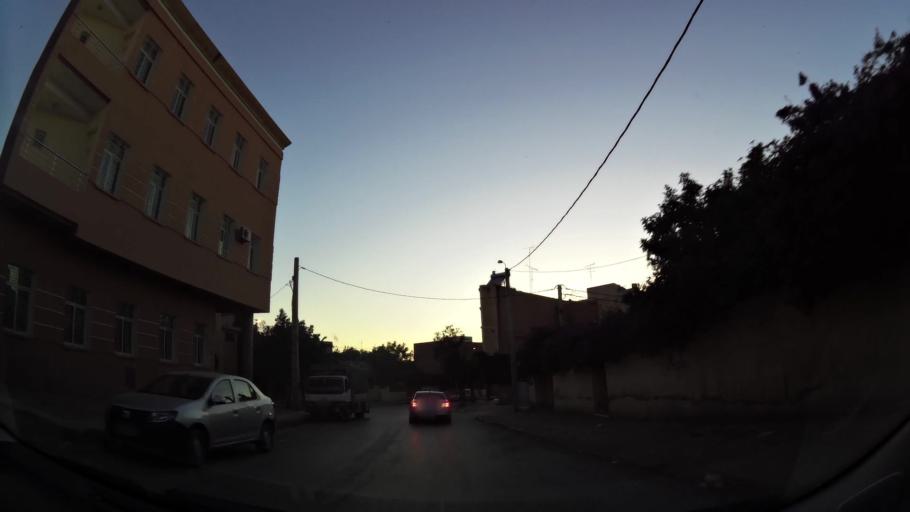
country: MA
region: Oriental
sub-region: Berkane-Taourirt
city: Berkane
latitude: 34.9215
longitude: -2.3282
